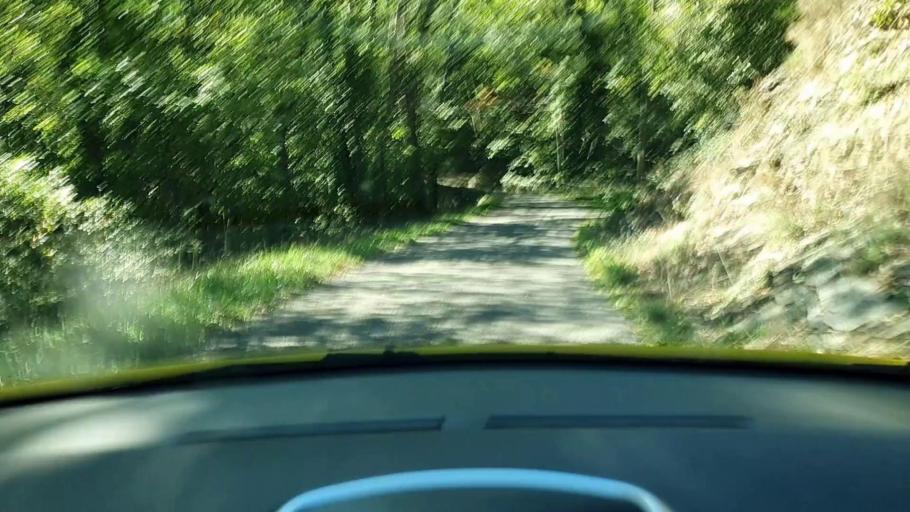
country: FR
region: Languedoc-Roussillon
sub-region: Departement du Gard
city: Le Vigan
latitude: 43.9918
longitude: 3.4550
